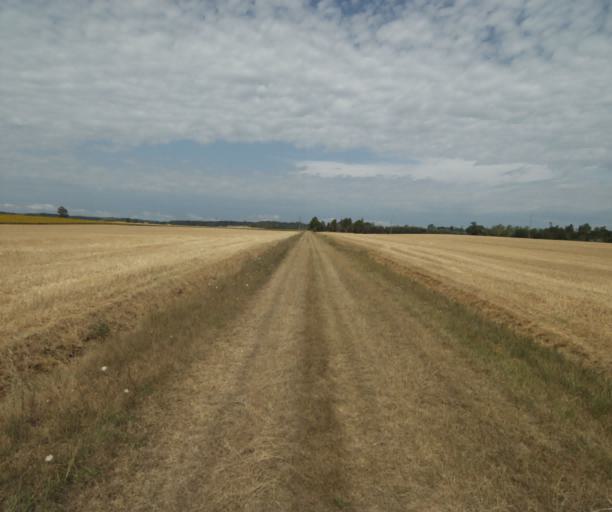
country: FR
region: Midi-Pyrenees
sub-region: Departement de la Haute-Garonne
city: Saint-Felix-Lauragais
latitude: 43.4180
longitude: 1.9173
